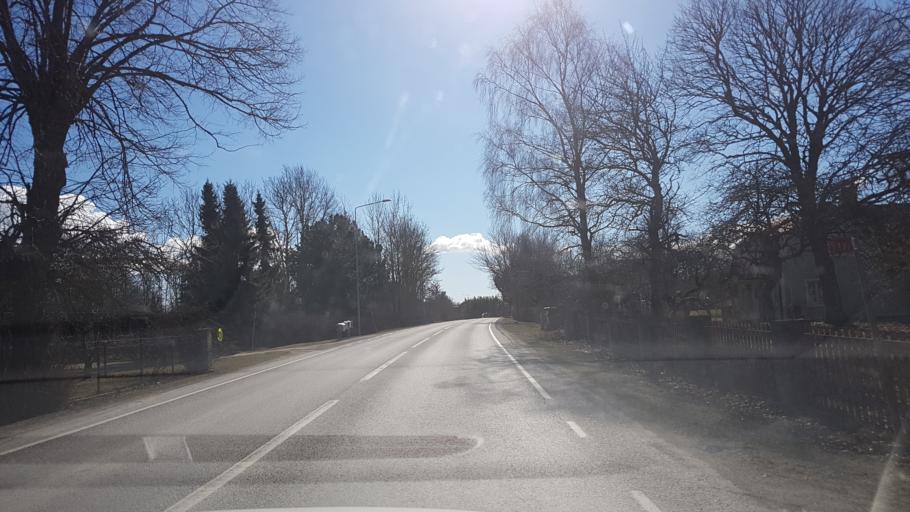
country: SE
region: Gotland
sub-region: Gotland
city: Visby
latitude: 57.5203
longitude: 18.4428
